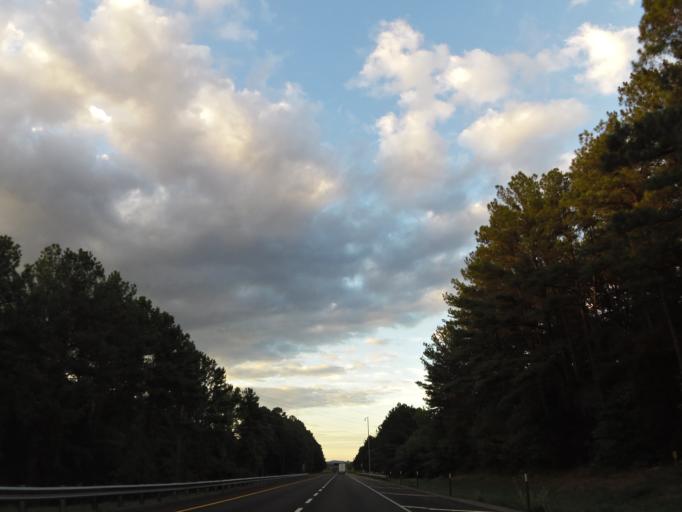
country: US
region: Tennessee
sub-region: Bradley County
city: Hopewell
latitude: 35.2801
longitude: -84.8187
